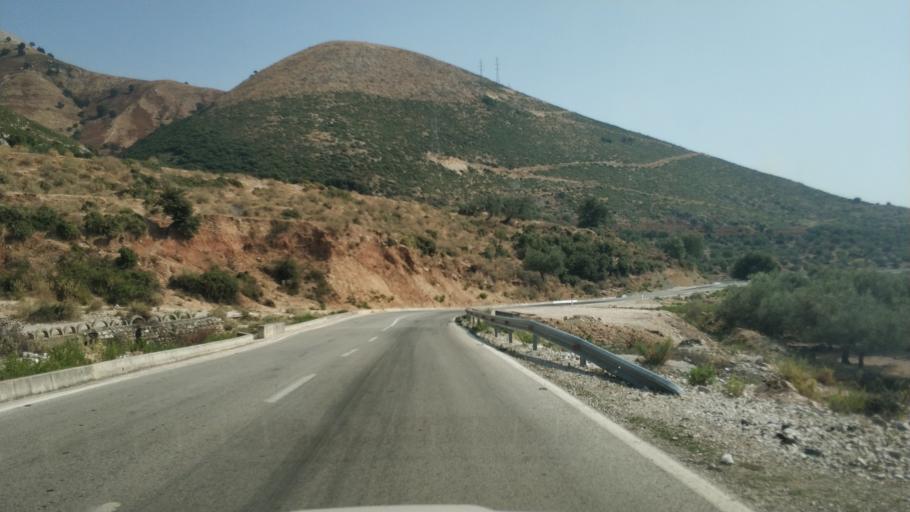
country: AL
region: Vlore
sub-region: Rrethi i Sarandes
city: Lukove
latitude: 40.0344
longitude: 19.8861
